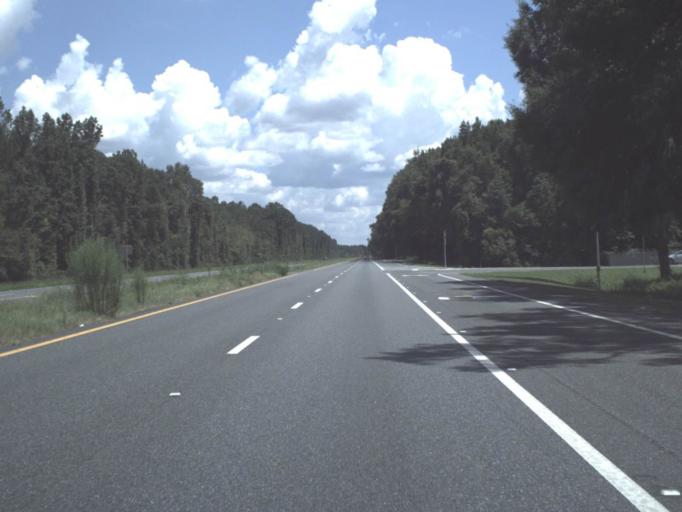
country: US
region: Florida
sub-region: Taylor County
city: Perry
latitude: 30.1994
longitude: -83.6542
